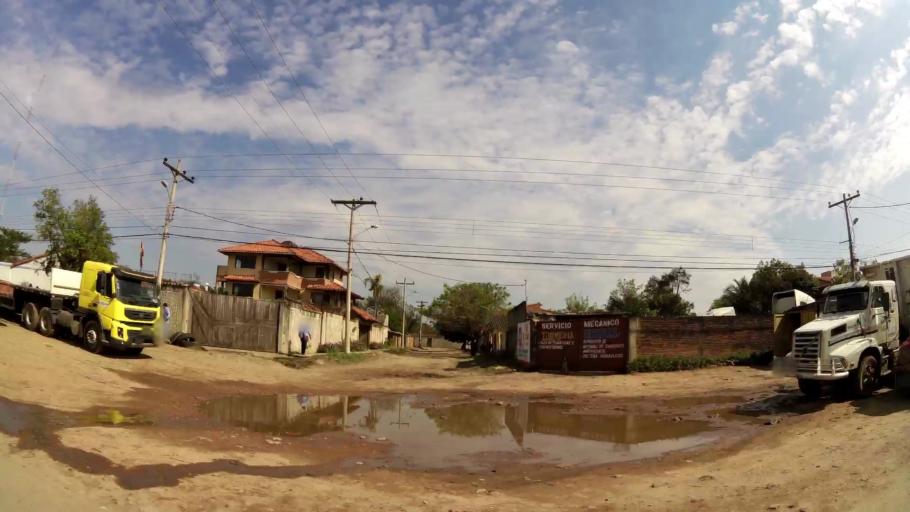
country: BO
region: Santa Cruz
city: Santa Cruz de la Sierra
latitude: -17.7262
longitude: -63.1577
